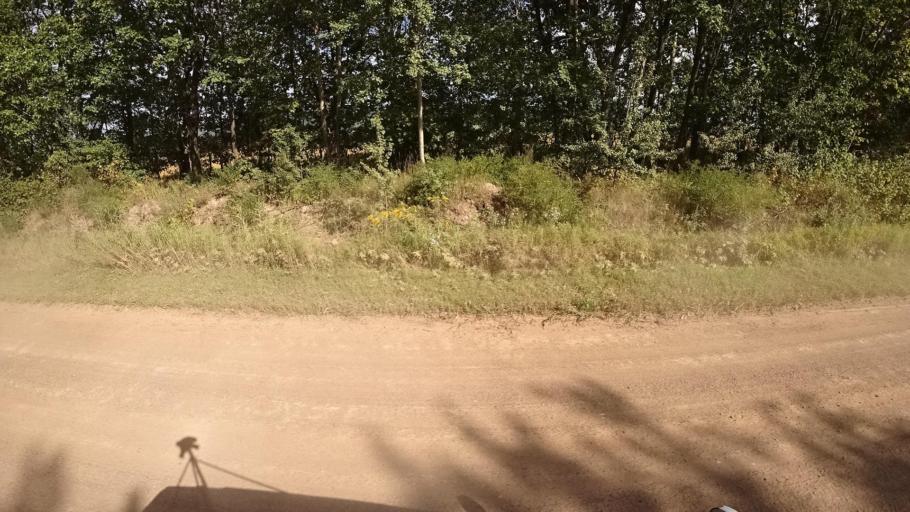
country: RU
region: Primorskiy
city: Yakovlevka
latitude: 44.4194
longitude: 133.5709
